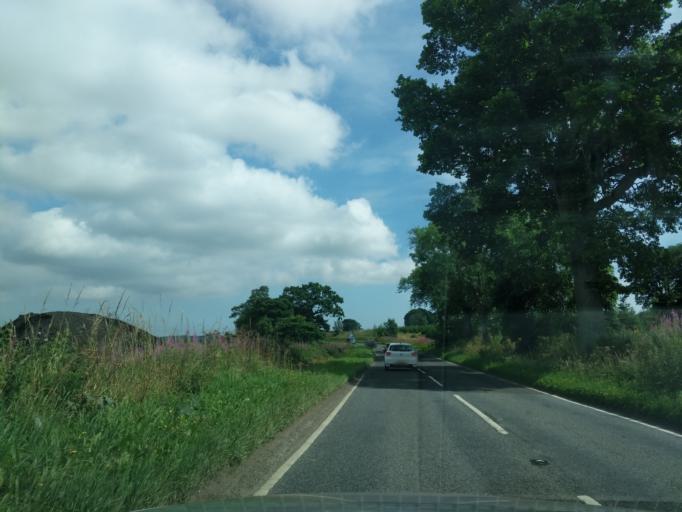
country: GB
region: Scotland
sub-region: Angus
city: Muirhead
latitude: 56.5011
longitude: -3.1086
